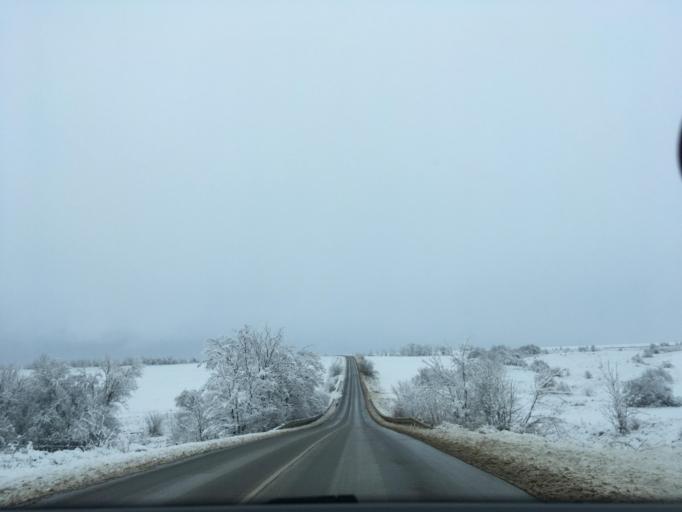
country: RU
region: Voronezj
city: Ol'khovatka
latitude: 50.2192
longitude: 39.2654
